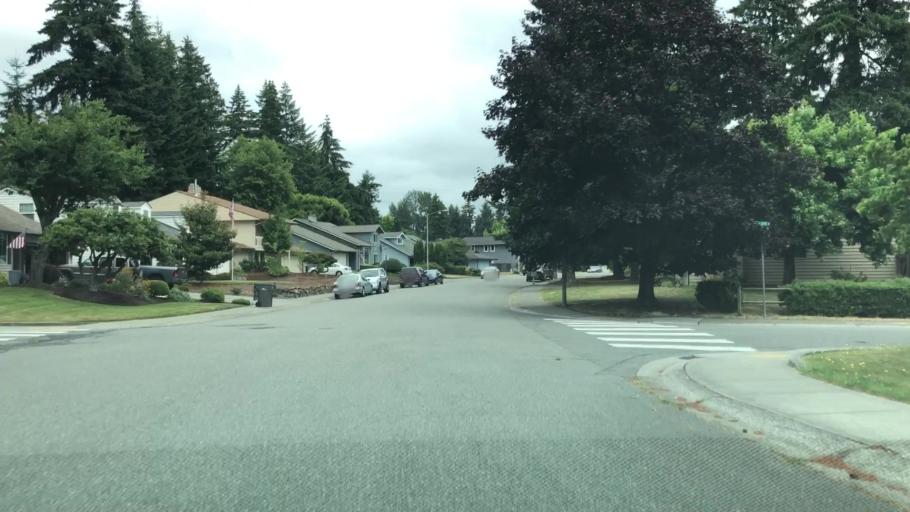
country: US
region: Washington
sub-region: King County
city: Kingsgate
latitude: 47.7261
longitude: -122.1793
